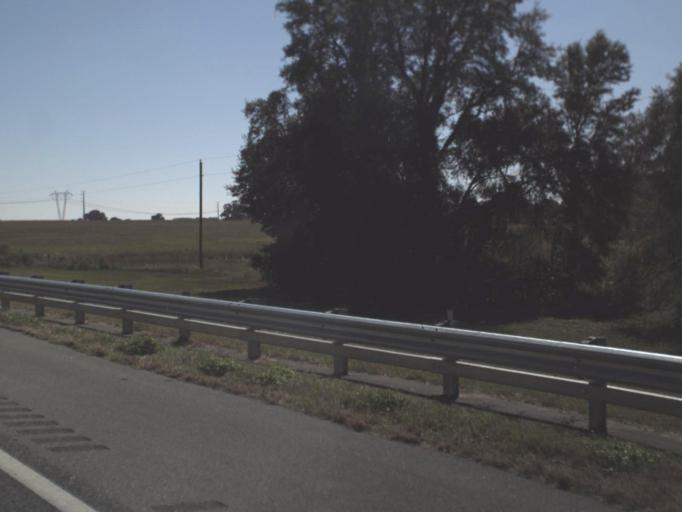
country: US
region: Florida
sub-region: Lake County
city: Leesburg
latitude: 28.7771
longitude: -81.9651
